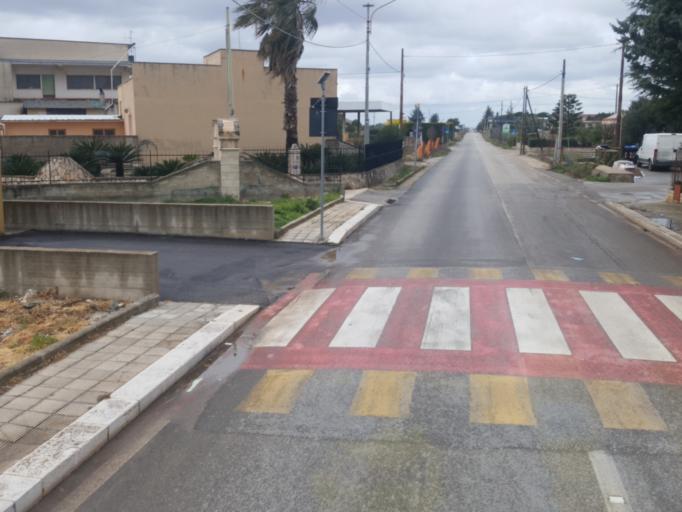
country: IT
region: Apulia
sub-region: Provincia di Bari
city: Turi
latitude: 40.9205
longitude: 17.0112
